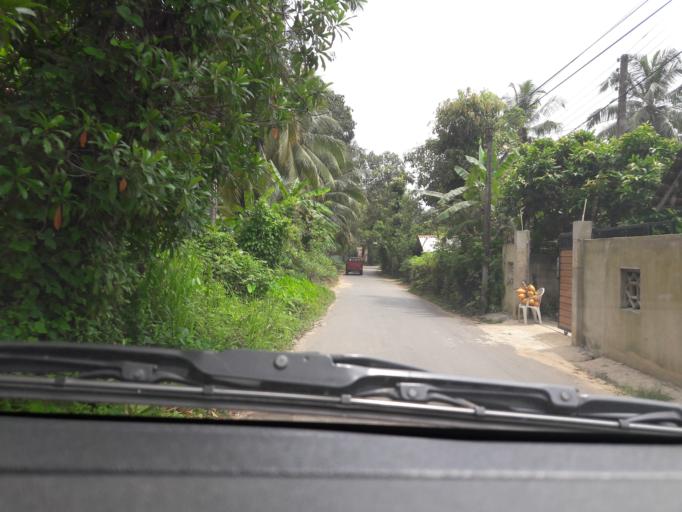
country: LK
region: Southern
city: Unawatuna
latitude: 6.0575
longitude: 80.2487
